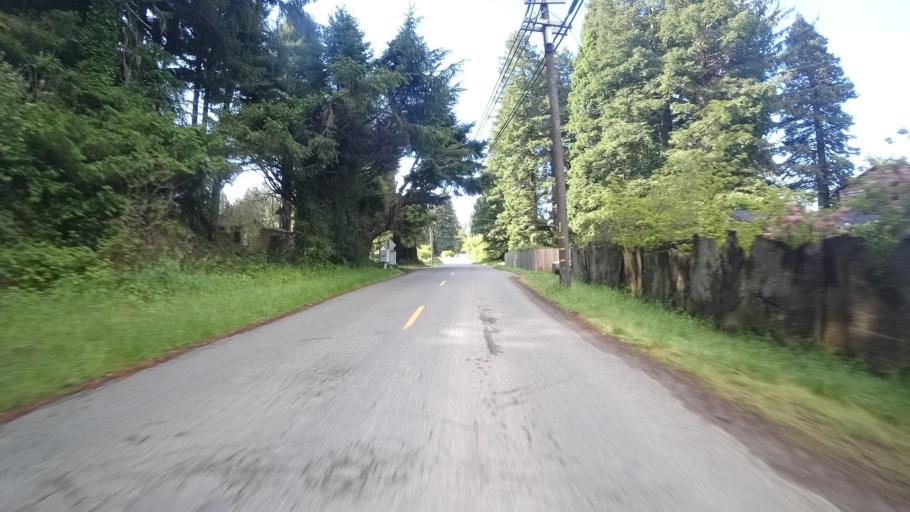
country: US
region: California
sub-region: Humboldt County
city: Westhaven-Moonstone
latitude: 41.0370
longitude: -124.1078
